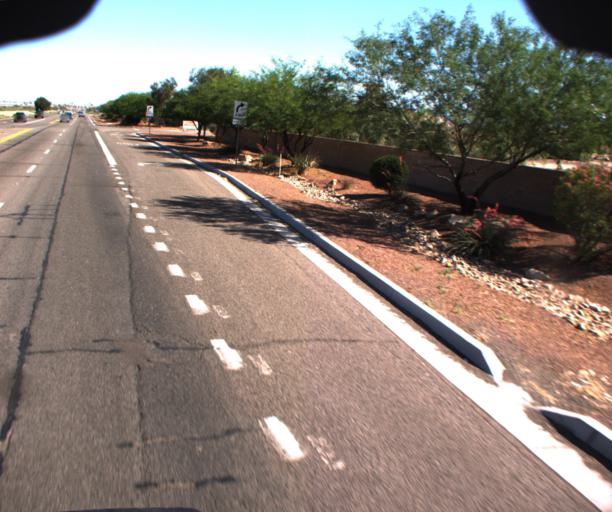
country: US
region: Arizona
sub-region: Mohave County
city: Mohave Valley
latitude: 34.9599
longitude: -114.5979
